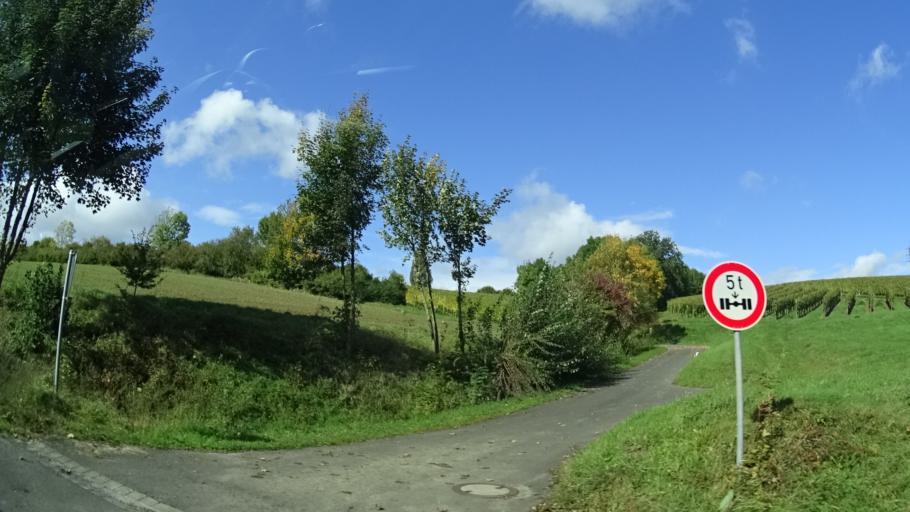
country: DE
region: Bavaria
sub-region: Regierungsbezirk Unterfranken
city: Buchbrunn
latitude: 49.7357
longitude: 10.1130
